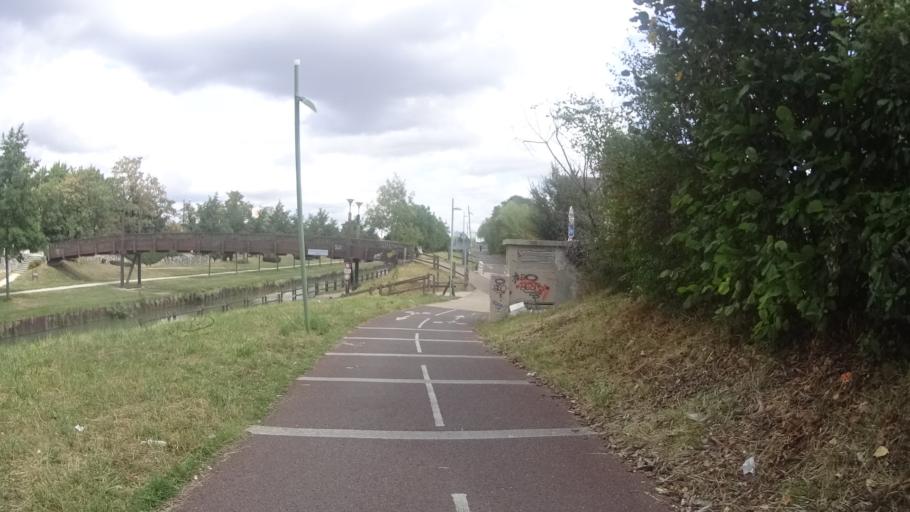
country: FR
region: Ile-de-France
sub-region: Departement de Seine-Saint-Denis
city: Sevran
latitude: 48.9275
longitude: 2.5168
